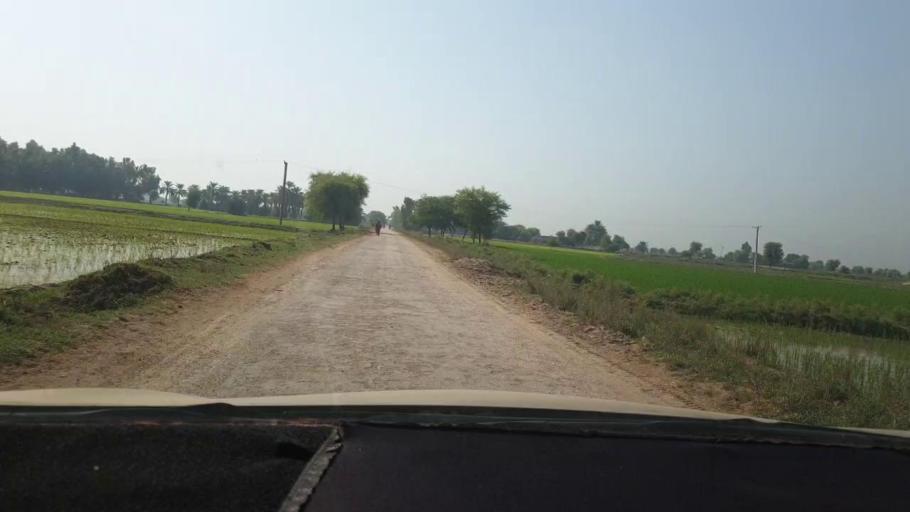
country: PK
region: Sindh
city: Miro Khan
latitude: 27.7280
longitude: 68.1193
